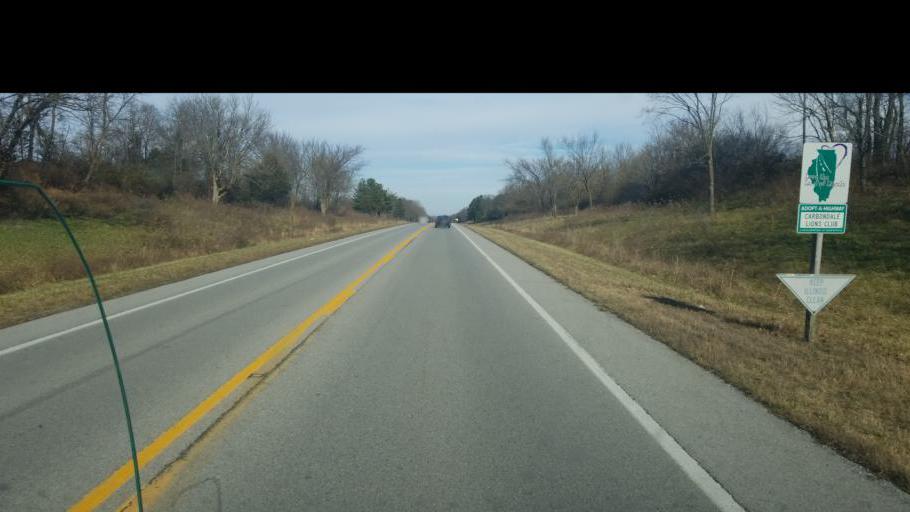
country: US
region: Illinois
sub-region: Jackson County
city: Carbondale
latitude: 37.6435
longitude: -89.2348
